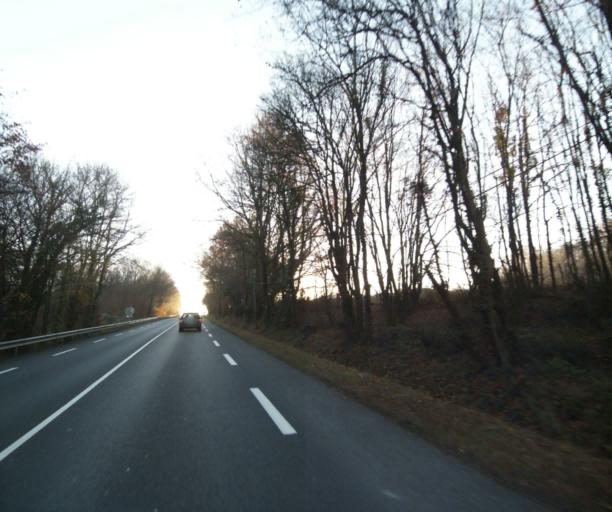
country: FR
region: Poitou-Charentes
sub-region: Departement de la Charente-Maritime
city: Chaniers
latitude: 45.7310
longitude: -0.5330
